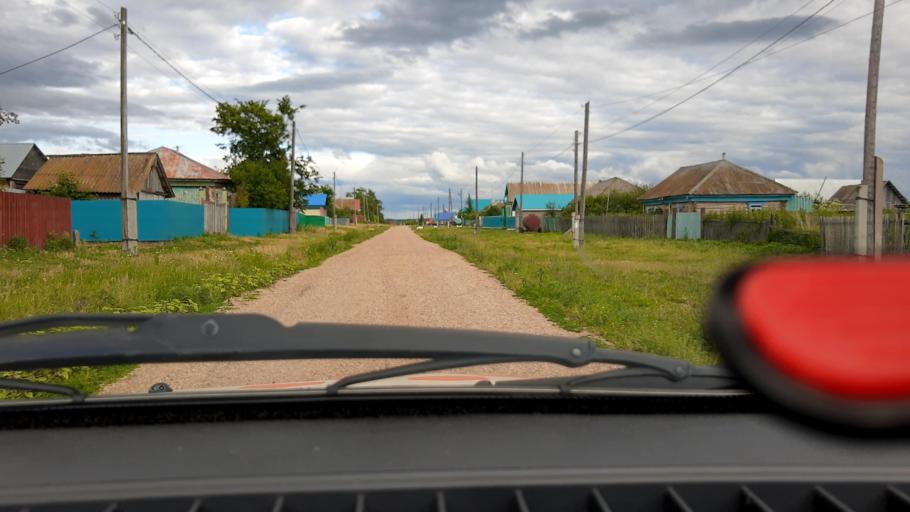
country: RU
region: Bashkortostan
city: Karmaskaly
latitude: 54.4205
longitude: 56.0244
